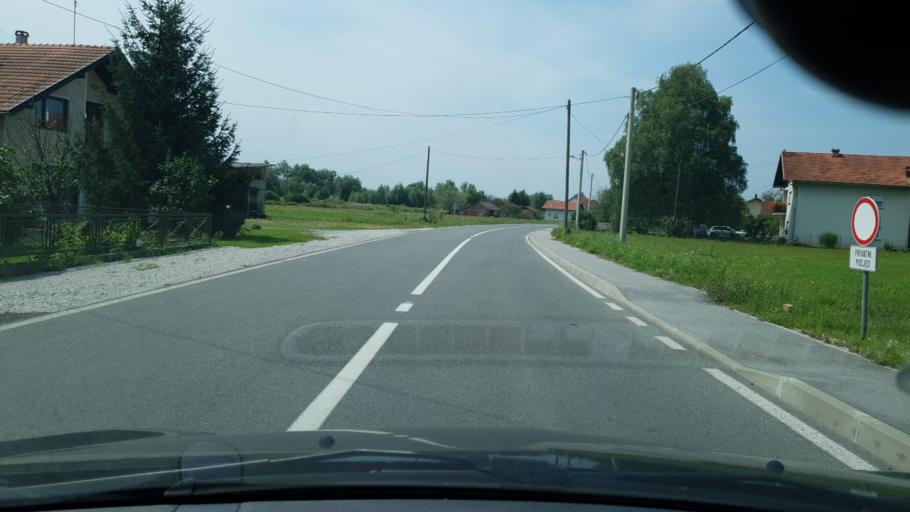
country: HR
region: Krapinsko-Zagorska
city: Zabok
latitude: 46.0216
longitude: 15.9498
